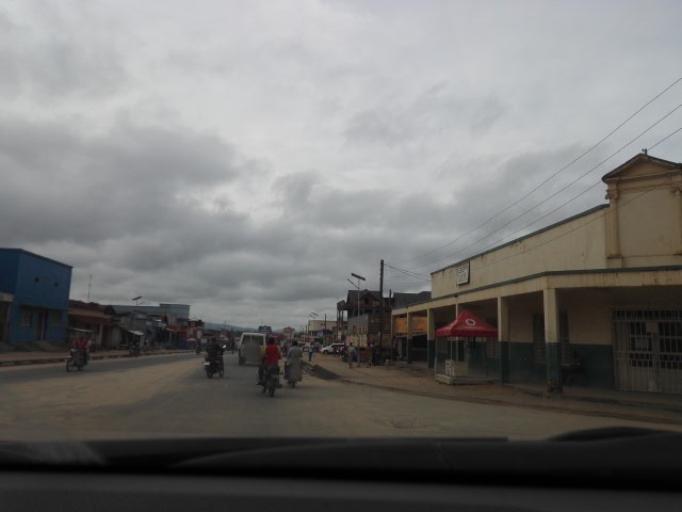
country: CD
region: Eastern Province
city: Bunia
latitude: 1.5554
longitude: 30.2479
